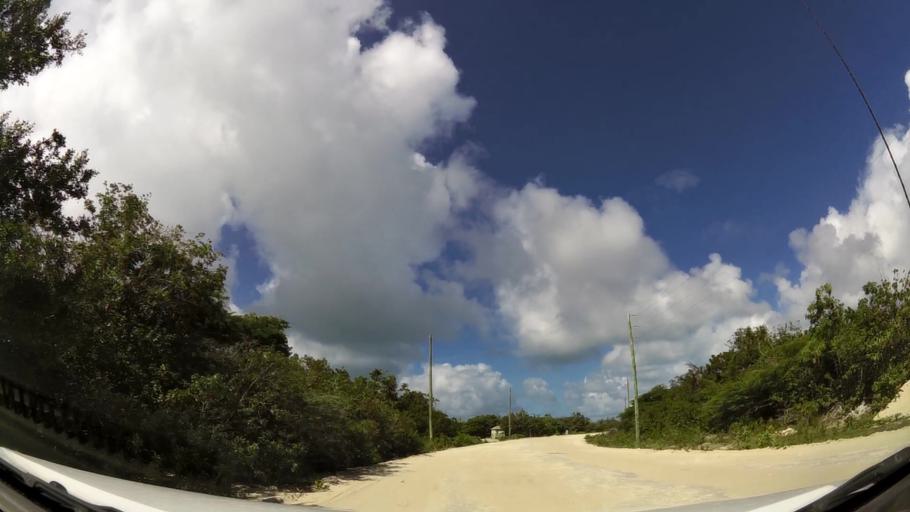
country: AG
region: Barbuda
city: Codrington
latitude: 17.5952
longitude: -61.8280
